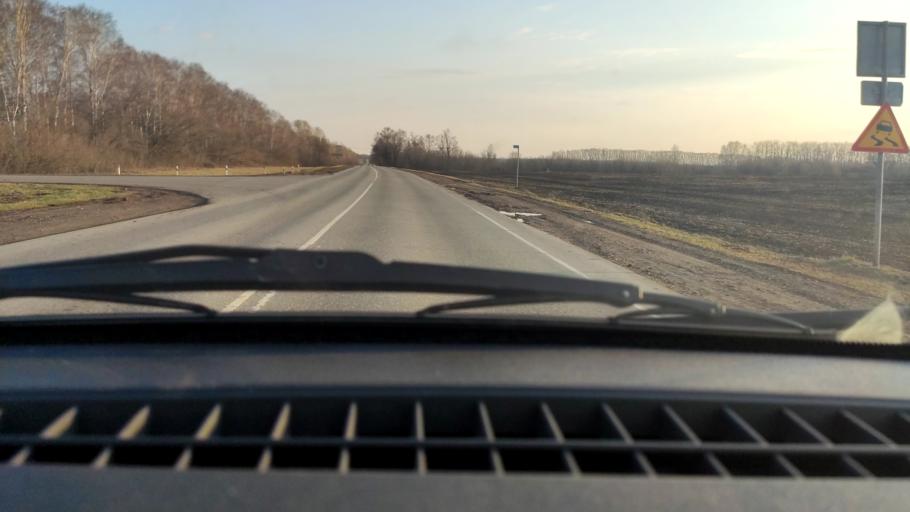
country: RU
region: Bashkortostan
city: Chishmy
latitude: 54.5250
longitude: 55.3007
